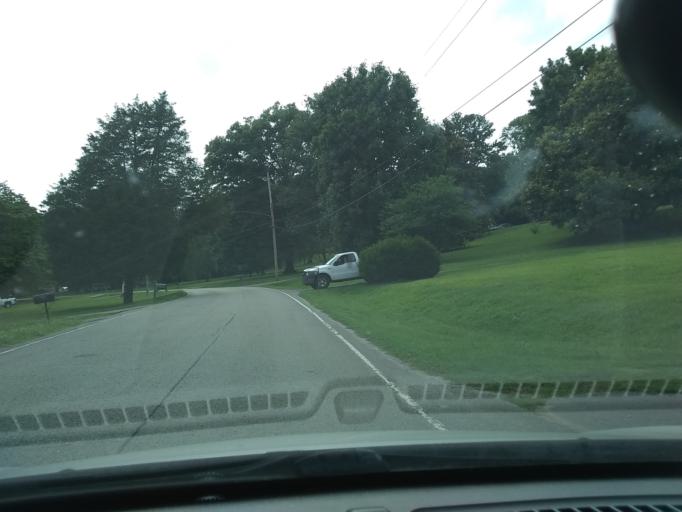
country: US
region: Tennessee
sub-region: Davidson County
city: Oak Hill
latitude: 36.1200
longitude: -86.7140
